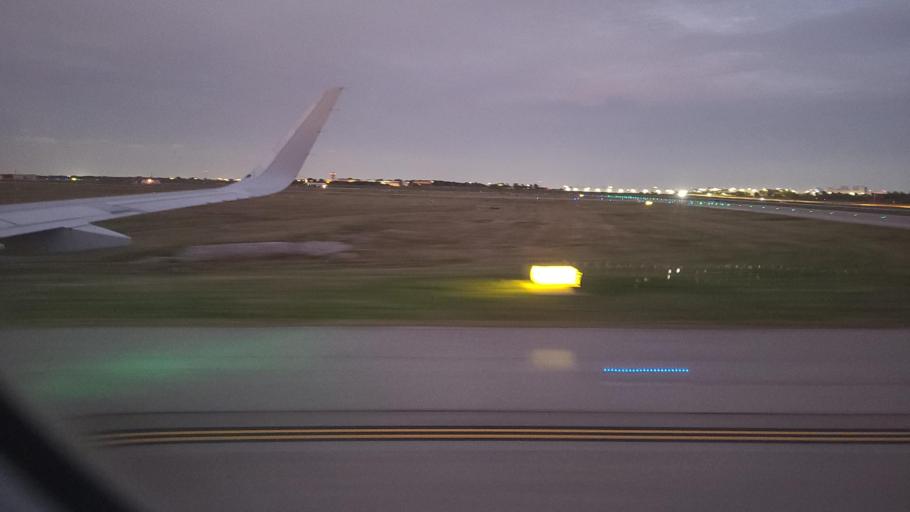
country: US
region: Texas
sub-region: Tarrant County
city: Euless
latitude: 32.8724
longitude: -97.0333
